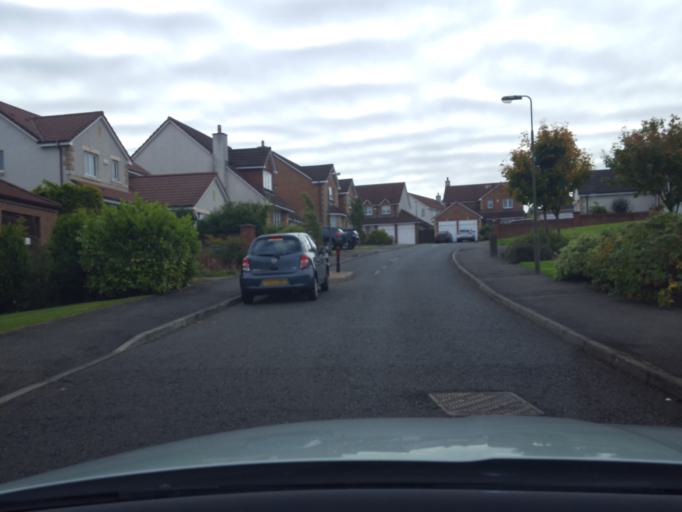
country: GB
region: Scotland
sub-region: West Lothian
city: Livingston
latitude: 55.8726
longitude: -3.5276
